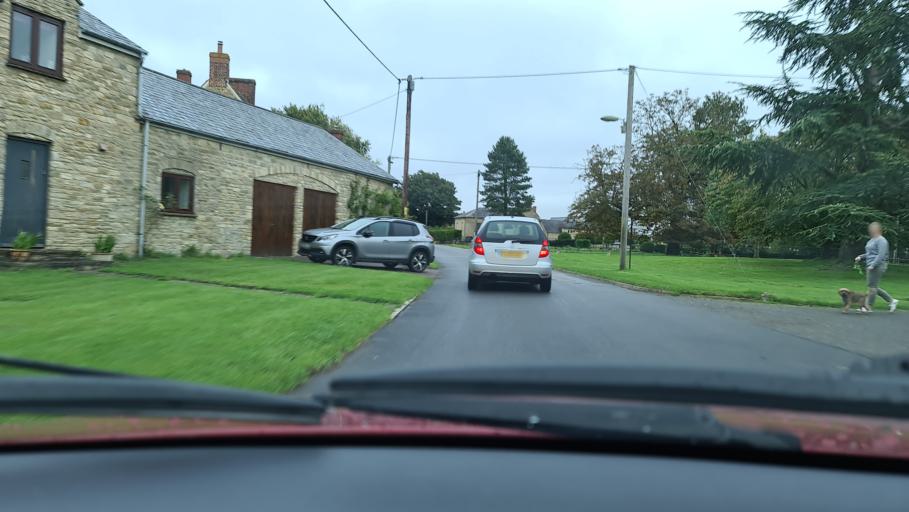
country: GB
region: England
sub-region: Oxfordshire
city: Somerton
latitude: 51.9609
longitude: -1.2399
